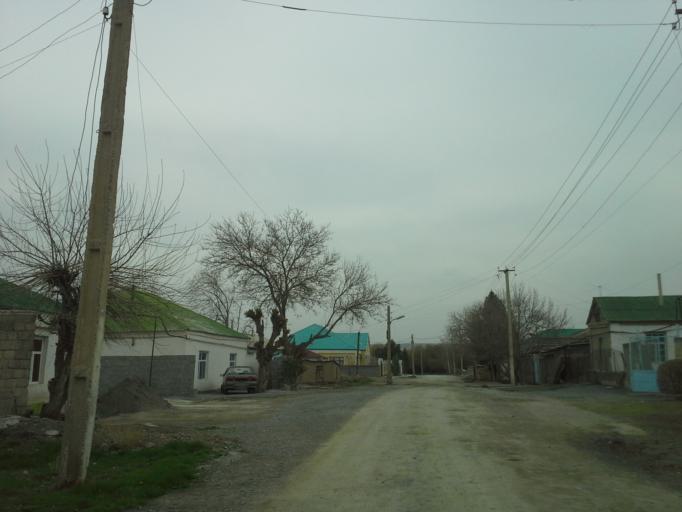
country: TM
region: Ahal
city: Abadan
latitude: 37.9702
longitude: 58.2198
